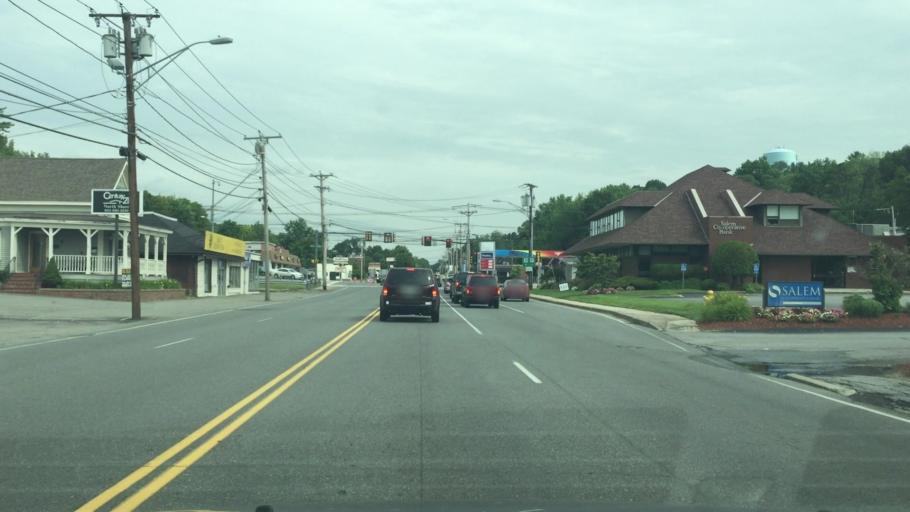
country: US
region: New Hampshire
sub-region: Rockingham County
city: Salem
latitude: 42.7789
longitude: -71.2278
